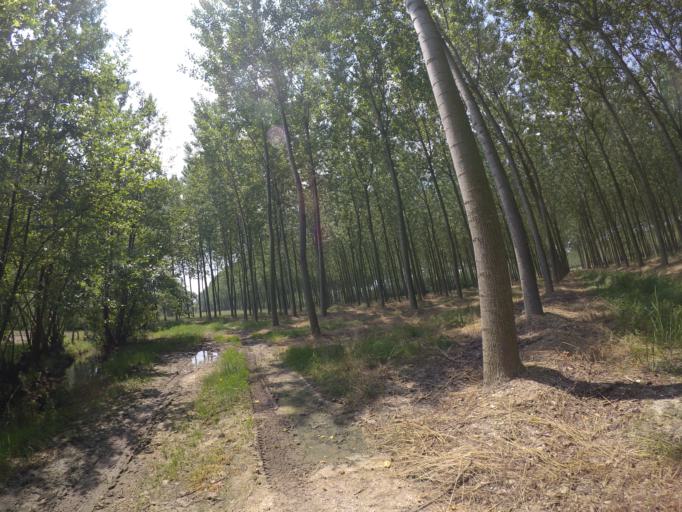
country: IT
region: Friuli Venezia Giulia
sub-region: Provincia di Udine
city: Bertiolo
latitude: 45.9126
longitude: 13.0378
